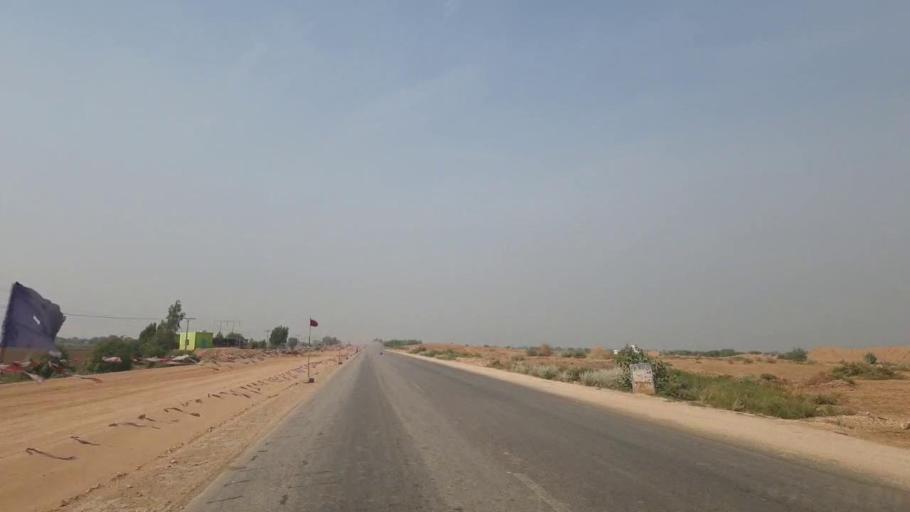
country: PK
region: Sindh
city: Sann
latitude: 26.1291
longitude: 68.0508
